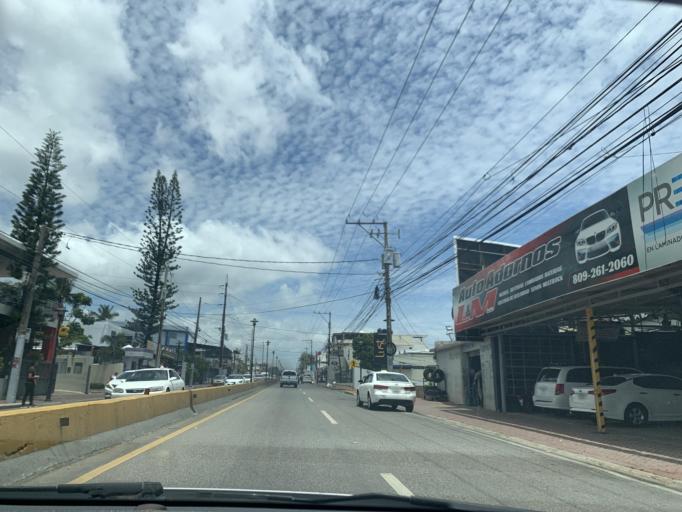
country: DO
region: Puerto Plata
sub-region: Puerto Plata
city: Puerto Plata
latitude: 19.7841
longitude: -70.6796
